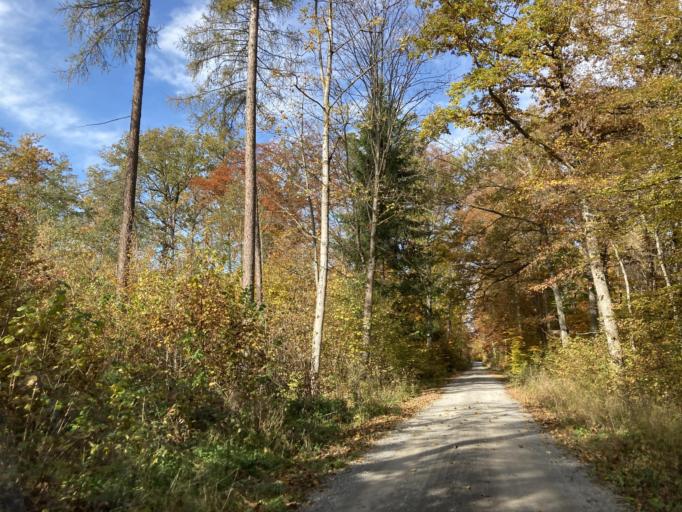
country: DE
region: Baden-Wuerttemberg
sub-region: Tuebingen Region
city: Rottenburg
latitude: 48.4419
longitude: 8.9626
